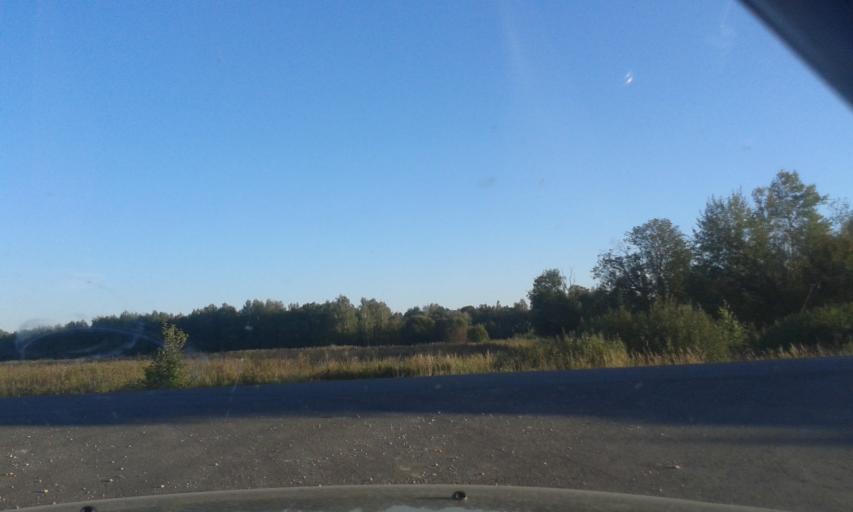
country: RU
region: Tula
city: Krapivna
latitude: 54.1144
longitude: 37.1531
